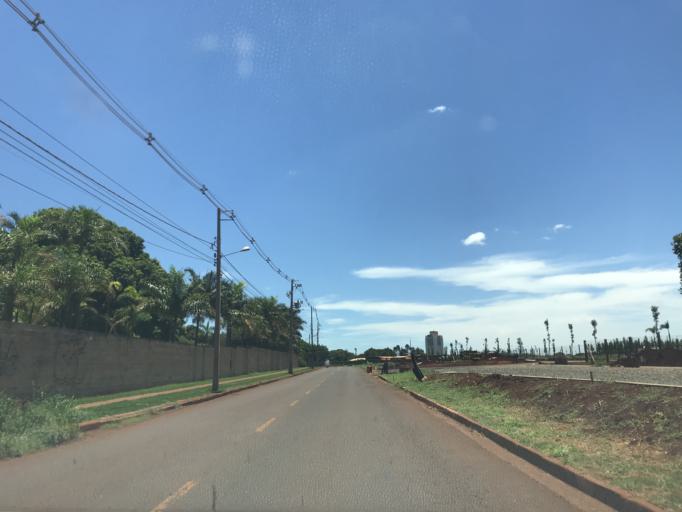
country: BR
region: Parana
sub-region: Sarandi
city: Sarandi
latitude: -23.4408
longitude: -51.9034
